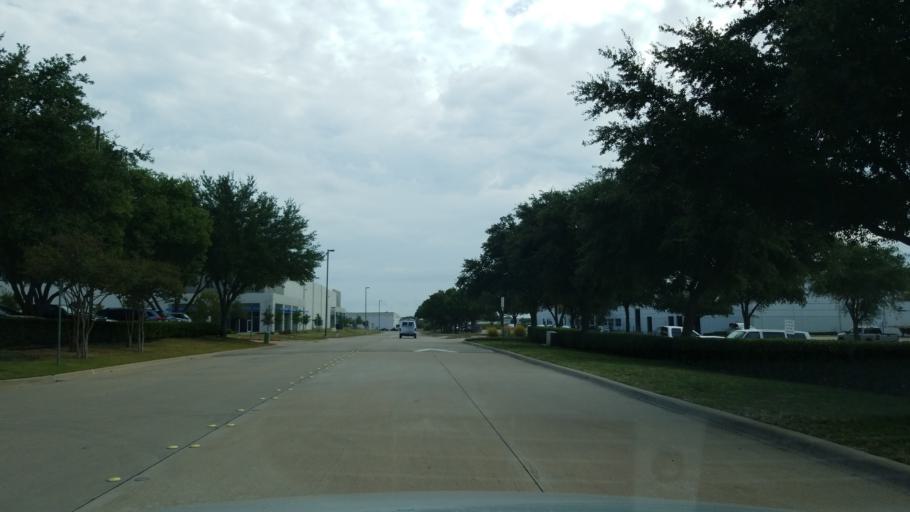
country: US
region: Texas
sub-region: Dallas County
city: Garland
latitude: 32.8916
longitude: -96.6914
